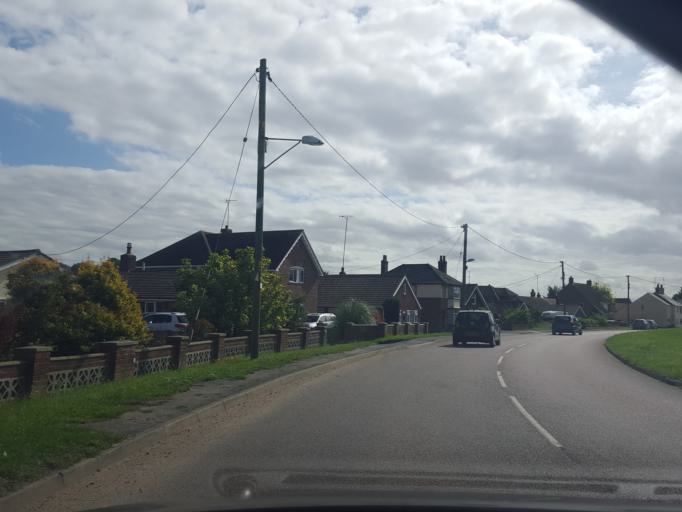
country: GB
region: England
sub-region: Suffolk
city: Shotley Gate
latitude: 51.9307
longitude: 1.2178
